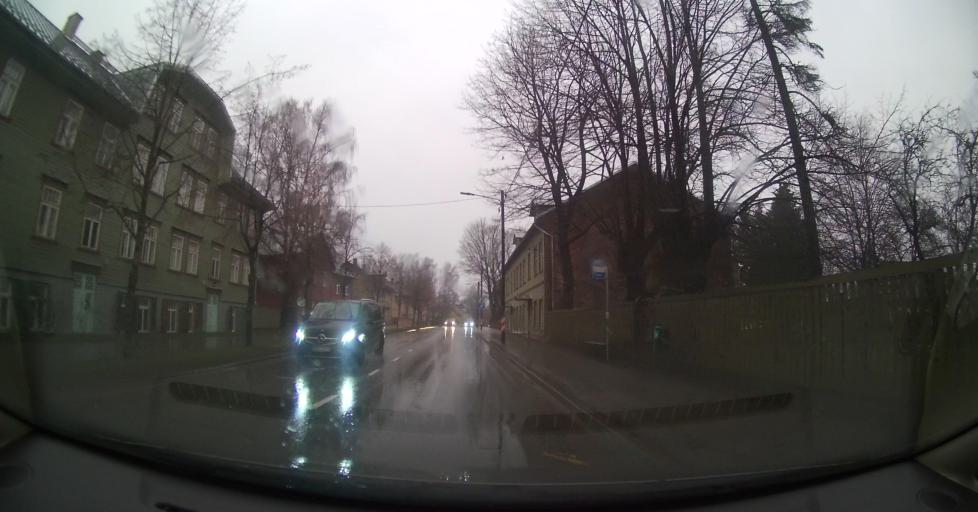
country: EE
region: Tartu
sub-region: Tartu linn
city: Tartu
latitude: 58.3632
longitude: 26.7306
